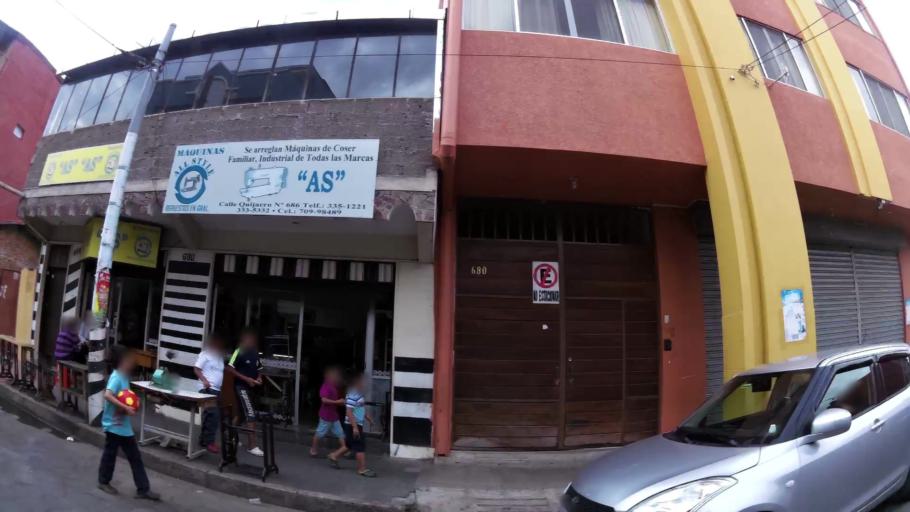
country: BO
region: Santa Cruz
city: Santa Cruz de la Sierra
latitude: -17.7758
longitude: -63.1786
